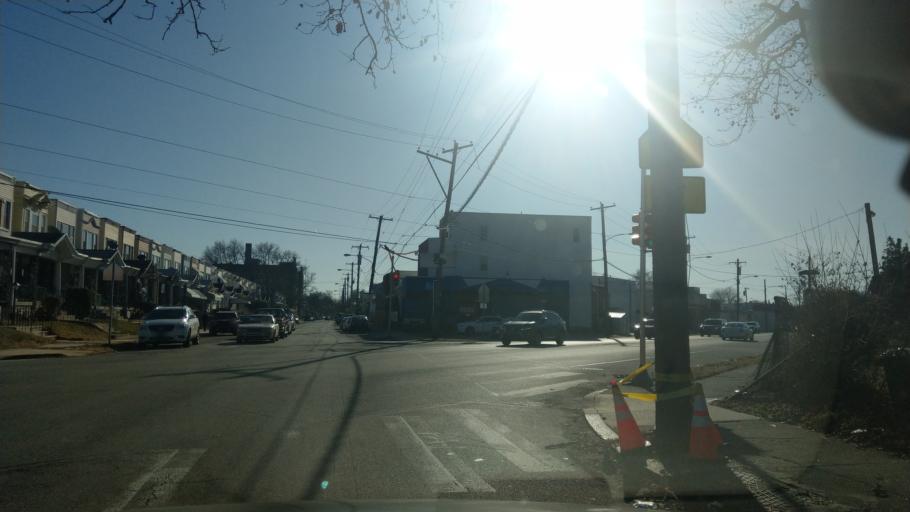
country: US
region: Pennsylvania
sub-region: Montgomery County
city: Wyncote
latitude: 40.0565
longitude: -75.1527
